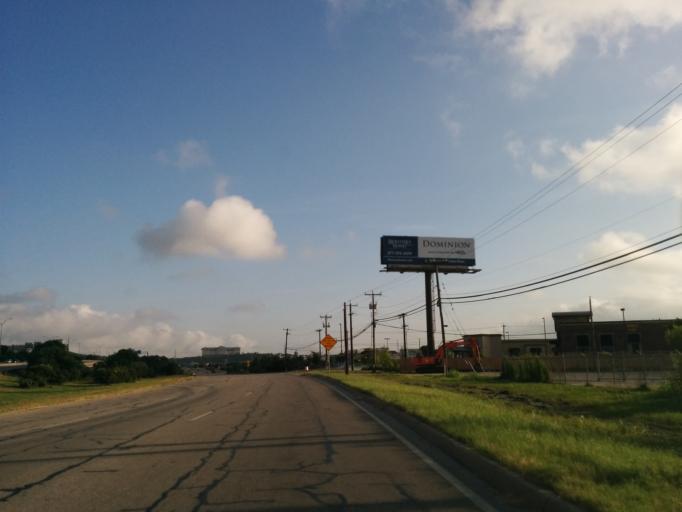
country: US
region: Texas
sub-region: Bexar County
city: Shavano Park
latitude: 29.6022
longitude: -98.6001
